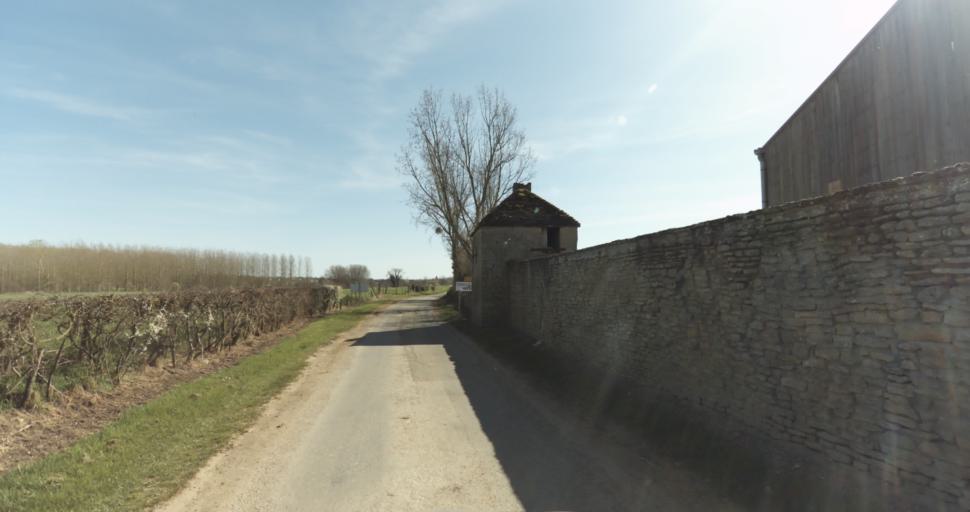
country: FR
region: Lower Normandy
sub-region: Departement du Calvados
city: Saint-Pierre-sur-Dives
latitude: 49.0499
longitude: -0.0269
